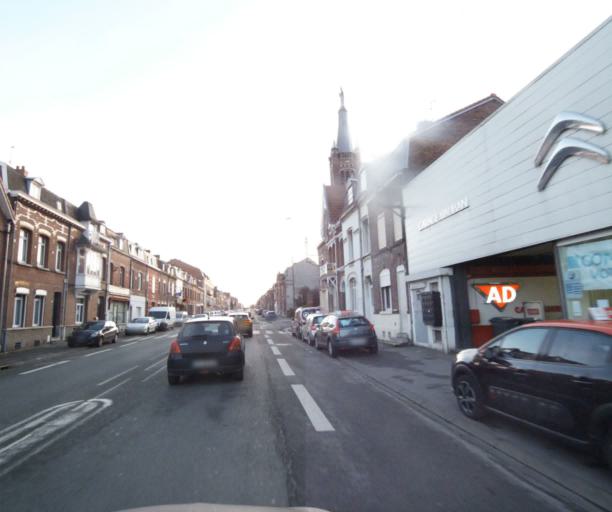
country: FR
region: Nord-Pas-de-Calais
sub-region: Departement du Nord
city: Anzin
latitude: 50.3635
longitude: 3.5085
